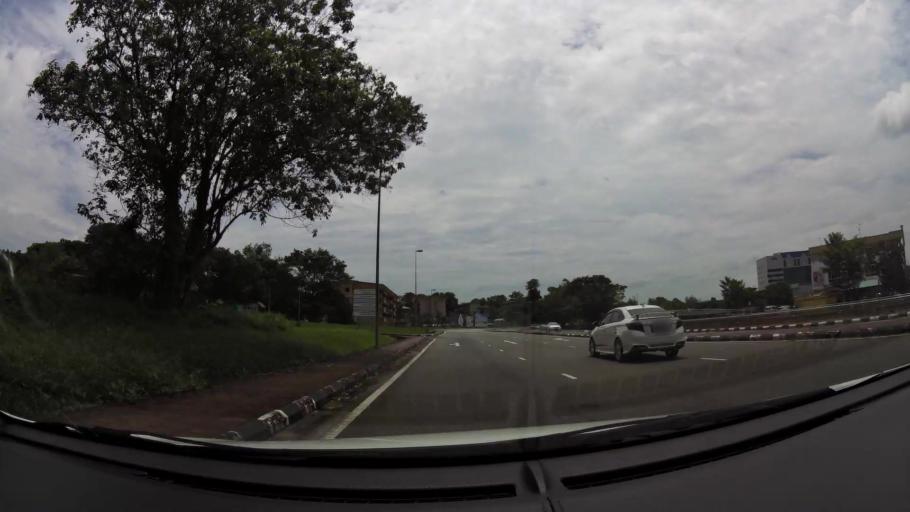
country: BN
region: Brunei and Muara
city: Bandar Seri Begawan
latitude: 4.9043
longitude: 114.9162
